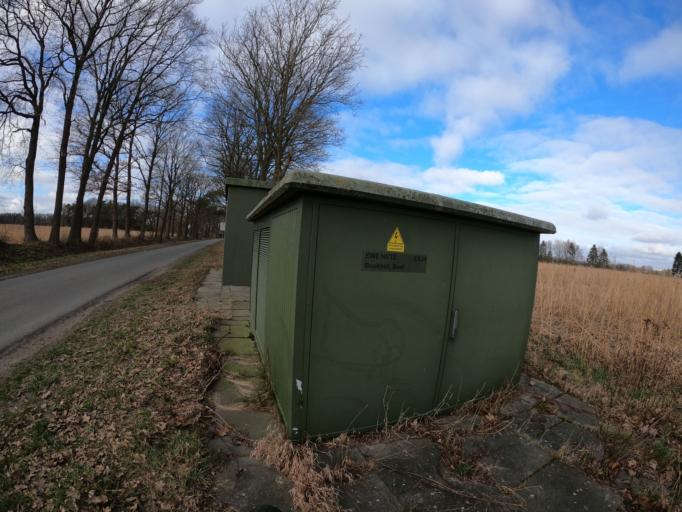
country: DE
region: Lower Saxony
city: Dohren
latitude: 52.6779
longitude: 7.5755
